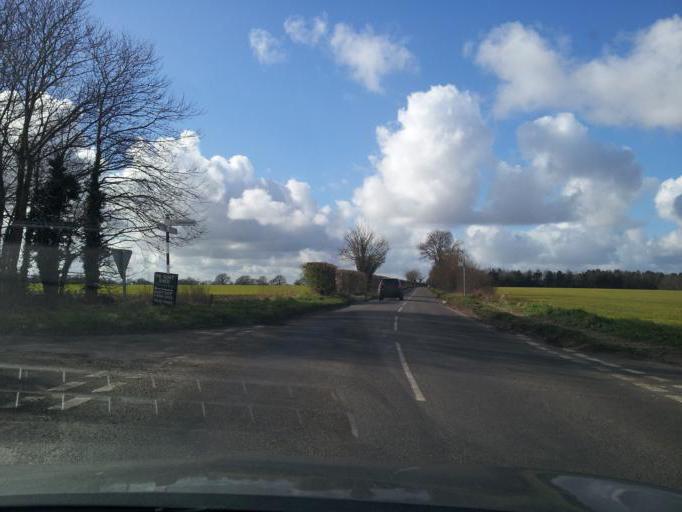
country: GB
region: England
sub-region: Norfolk
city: Mattishall
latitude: 52.6582
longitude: 1.1092
